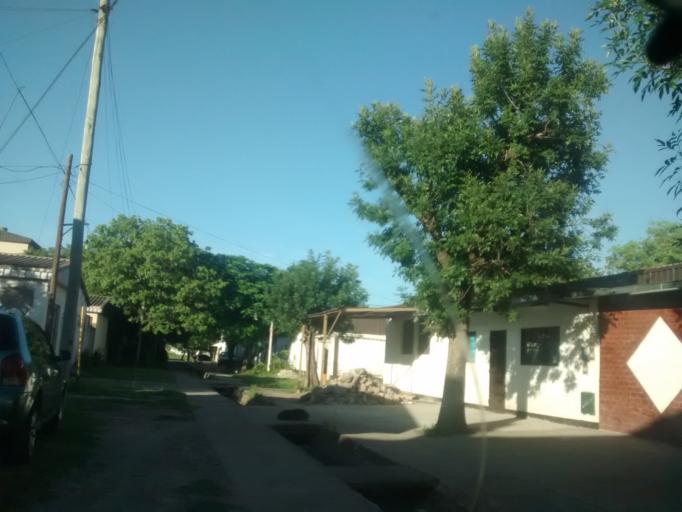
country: AR
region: Chaco
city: Resistencia
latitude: -27.4583
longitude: -59.0197
